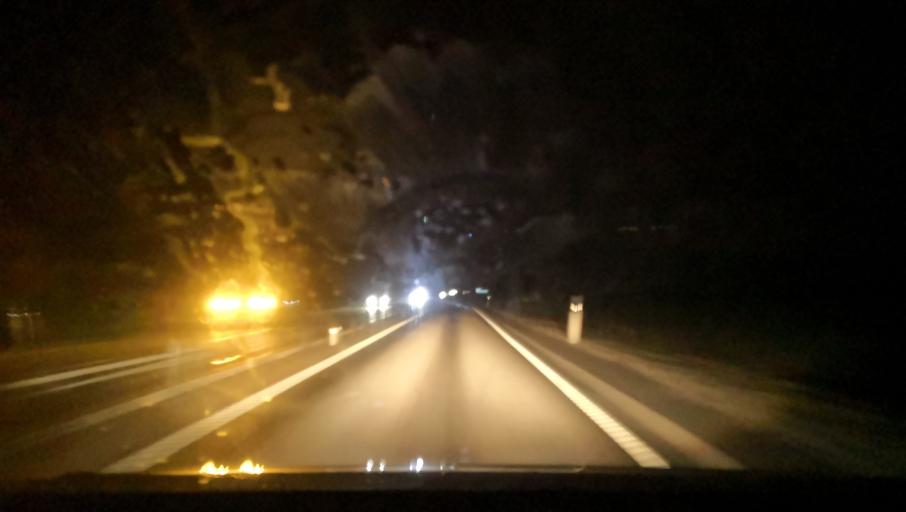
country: SE
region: Uppsala
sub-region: Enkopings Kommun
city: Orsundsbro
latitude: 59.6852
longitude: 17.2776
